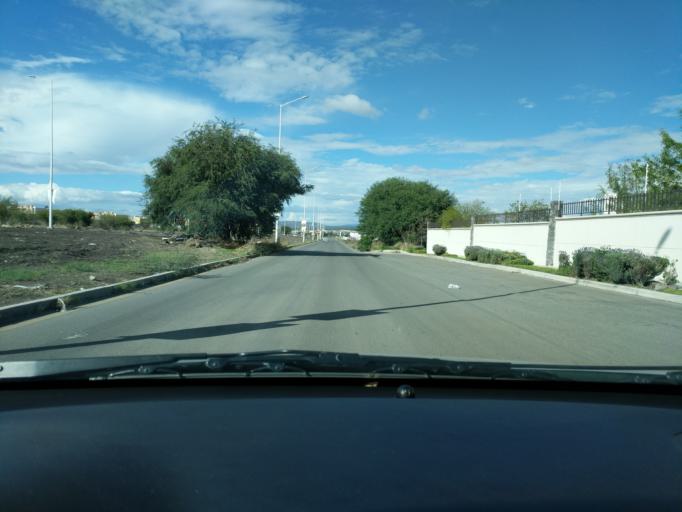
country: MX
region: Queretaro
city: El Colorado
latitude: 20.5867
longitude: -100.2845
